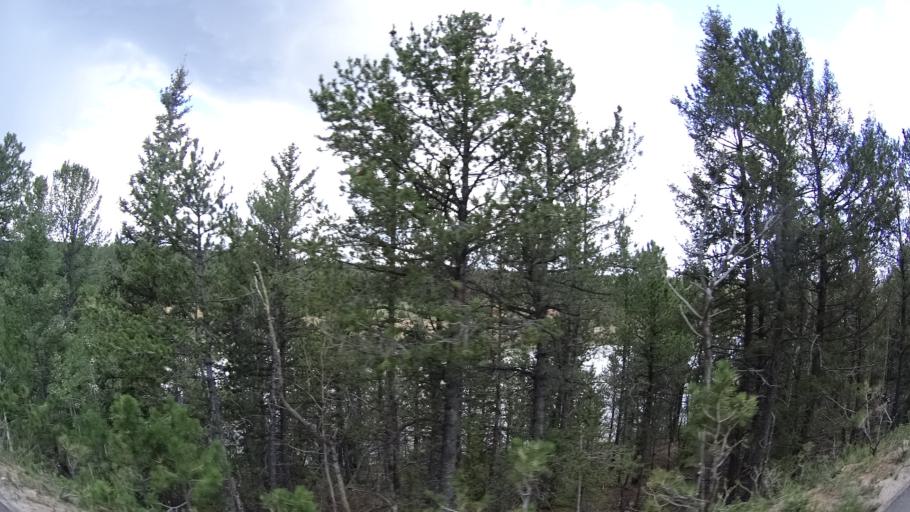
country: US
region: Colorado
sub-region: El Paso County
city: Cascade-Chipita Park
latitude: 38.9137
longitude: -105.0302
